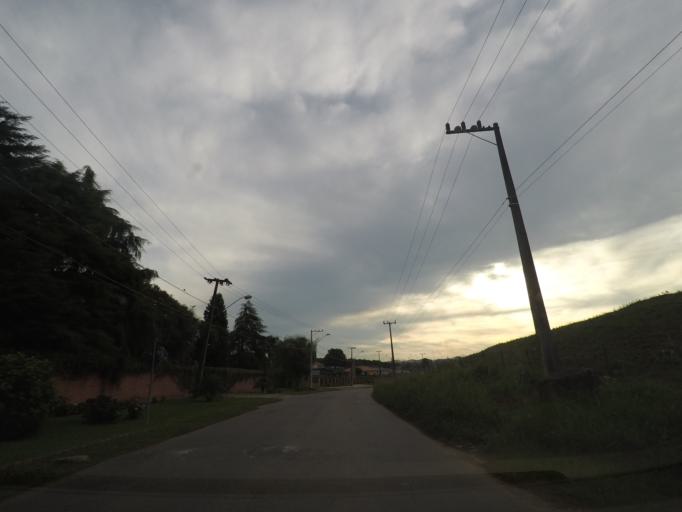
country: BR
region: Parana
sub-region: Colombo
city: Colombo
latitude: -25.2882
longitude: -49.1940
